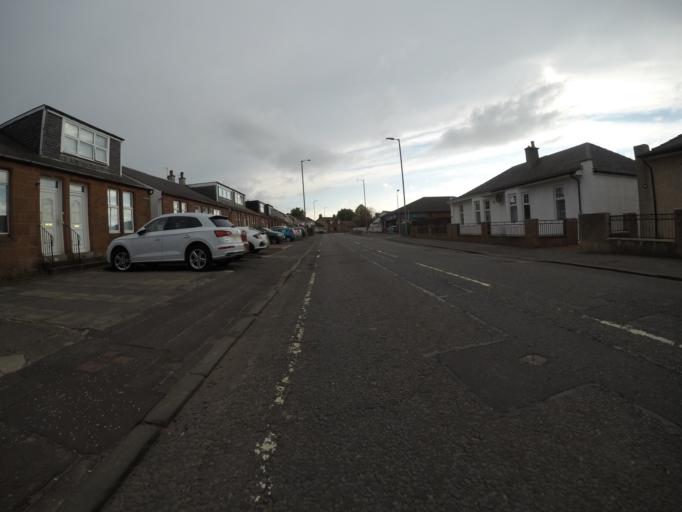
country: GB
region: Scotland
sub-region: North Ayrshire
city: Dreghorn
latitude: 55.6076
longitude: -4.6217
